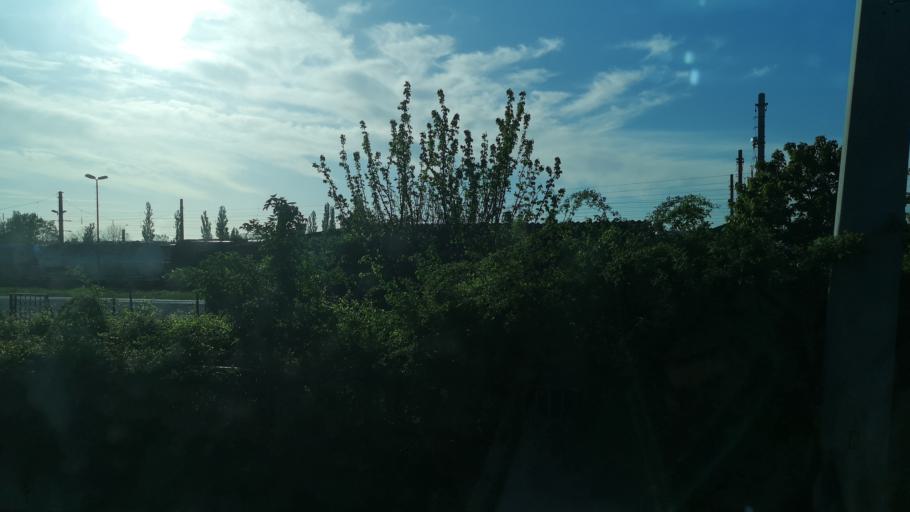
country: AT
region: Lower Austria
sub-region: Politischer Bezirk Wien-Umgebung
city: Schwechat
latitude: 48.1440
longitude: 16.4623
